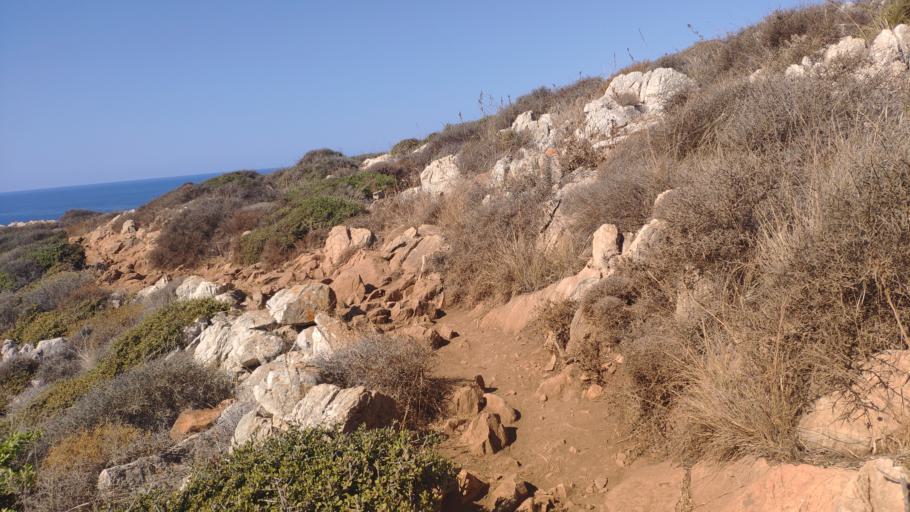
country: GR
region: Peloponnese
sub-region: Nomos Lakonias
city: Gytheio
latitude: 36.3900
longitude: 22.4828
